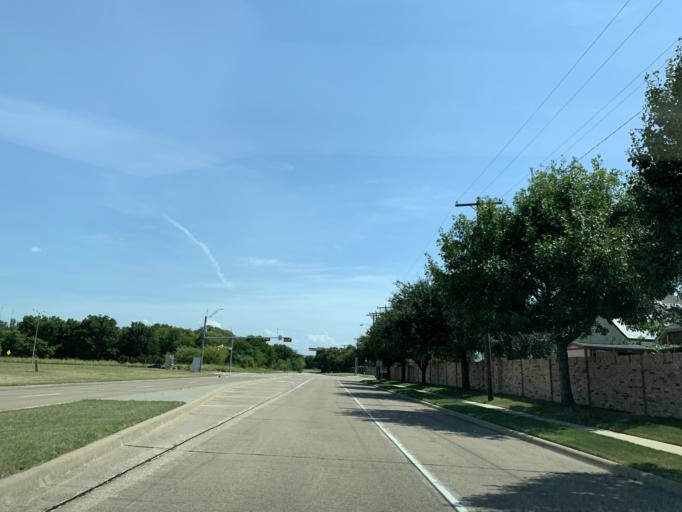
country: US
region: Texas
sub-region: Dallas County
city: Cedar Hill
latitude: 32.6448
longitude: -97.0143
